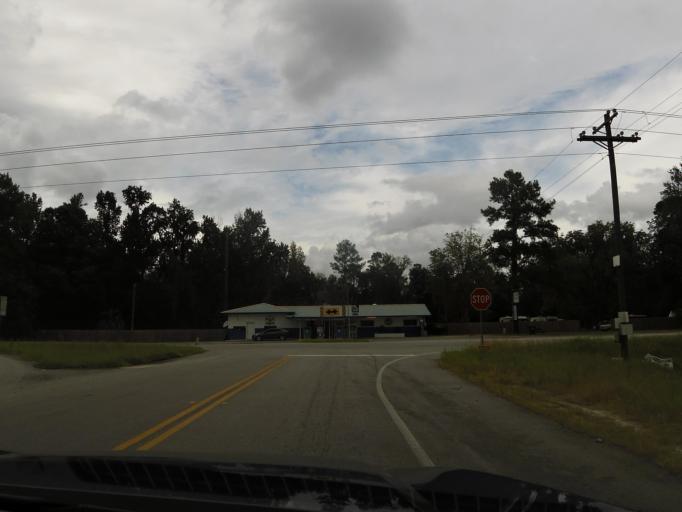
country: US
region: Florida
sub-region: Baker County
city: Macclenny
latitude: 30.5185
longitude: -82.2247
